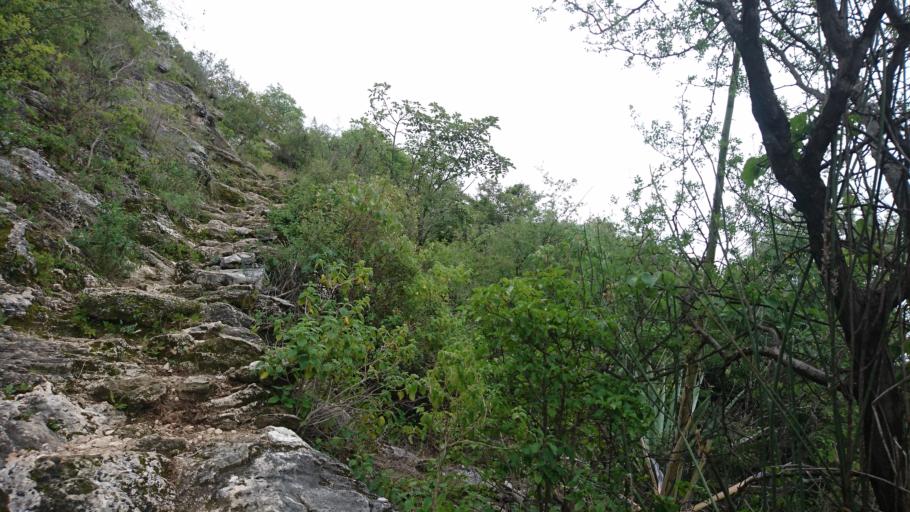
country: MX
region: Oaxaca
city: San Lorenzo Albarradas
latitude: 16.8673
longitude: -96.2744
